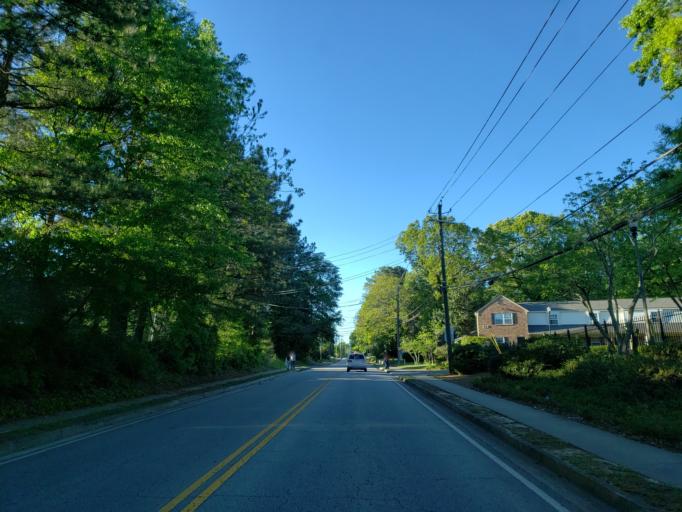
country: US
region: Georgia
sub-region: Cobb County
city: Fair Oaks
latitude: 33.9043
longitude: -84.5400
